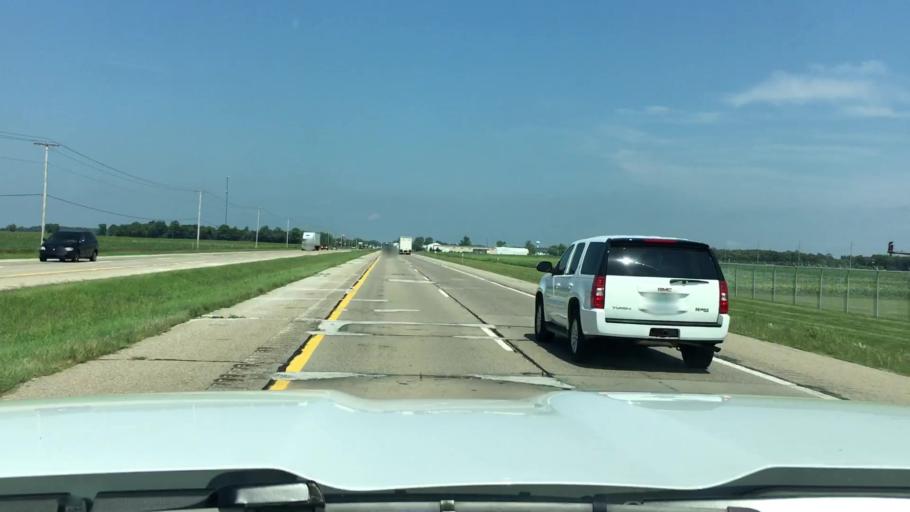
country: US
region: Michigan
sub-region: Kalamazoo County
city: Schoolcraft
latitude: 42.0818
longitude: -85.6366
